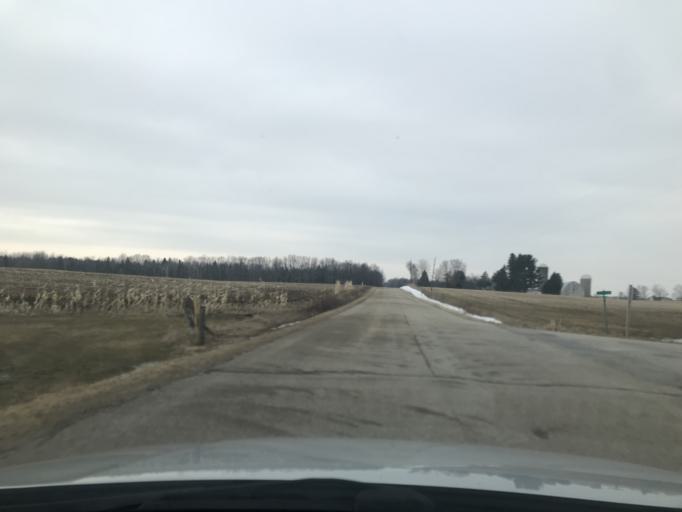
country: US
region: Wisconsin
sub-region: Marinette County
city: Peshtigo
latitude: 45.1234
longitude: -88.0079
